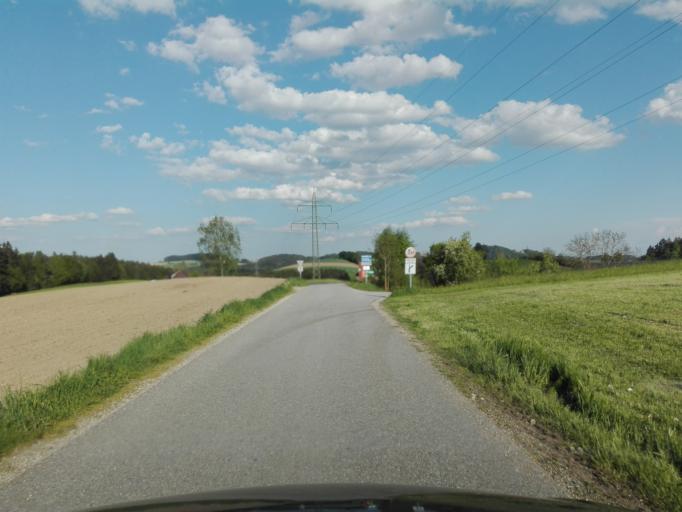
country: AT
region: Upper Austria
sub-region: Politischer Bezirk Rohrbach
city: Atzesberg
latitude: 48.4625
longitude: 13.8911
